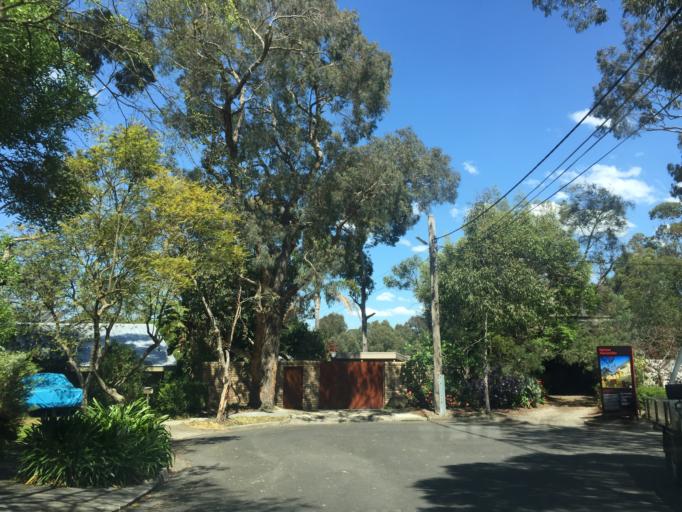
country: AU
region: Victoria
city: Alphington
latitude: -37.7863
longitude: 145.0324
